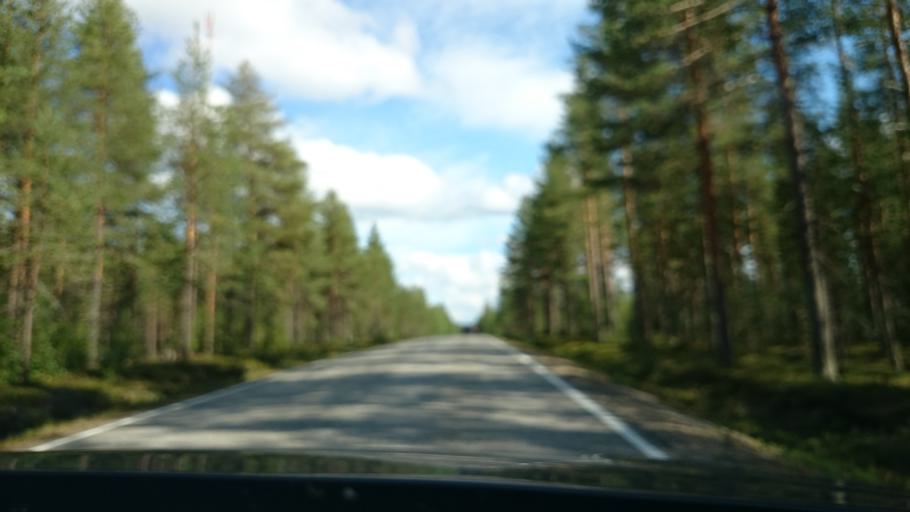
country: FI
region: Kainuu
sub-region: Kehys-Kainuu
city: Suomussalmi
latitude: 64.7512
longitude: 29.4232
